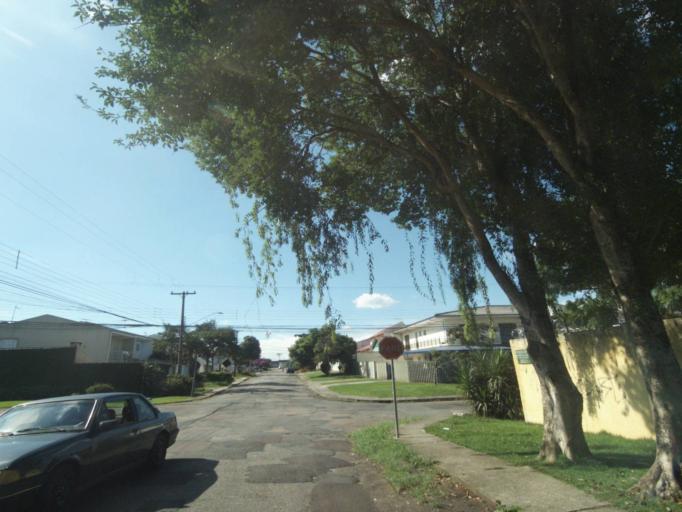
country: BR
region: Parana
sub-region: Pinhais
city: Pinhais
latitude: -25.4553
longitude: -49.2112
